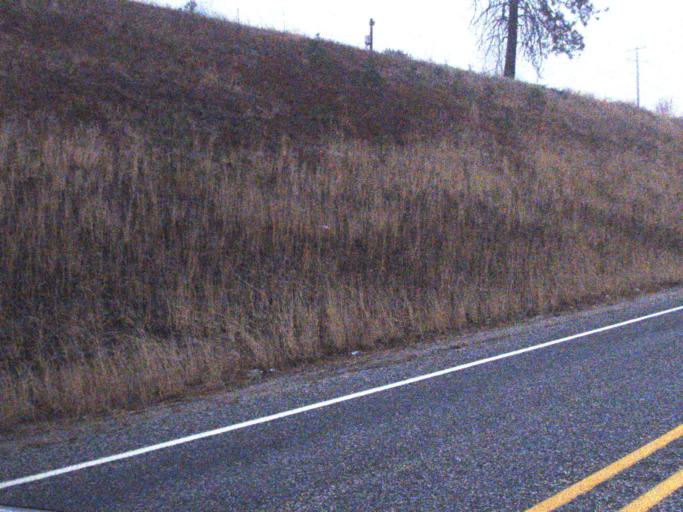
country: US
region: Washington
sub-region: Stevens County
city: Kettle Falls
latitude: 48.6979
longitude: -118.1264
